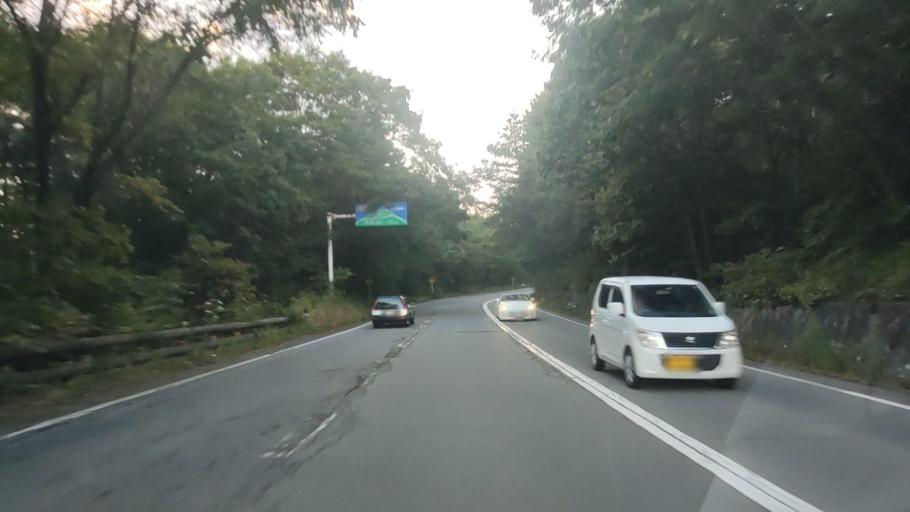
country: JP
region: Nagano
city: Komoro
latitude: 36.3886
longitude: 138.5858
